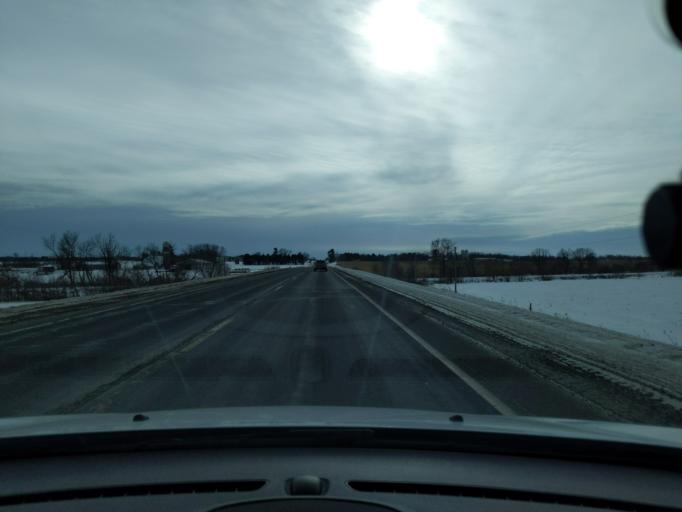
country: US
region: Wisconsin
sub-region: Barron County
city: Turtle Lake
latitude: 45.3870
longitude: -92.1667
